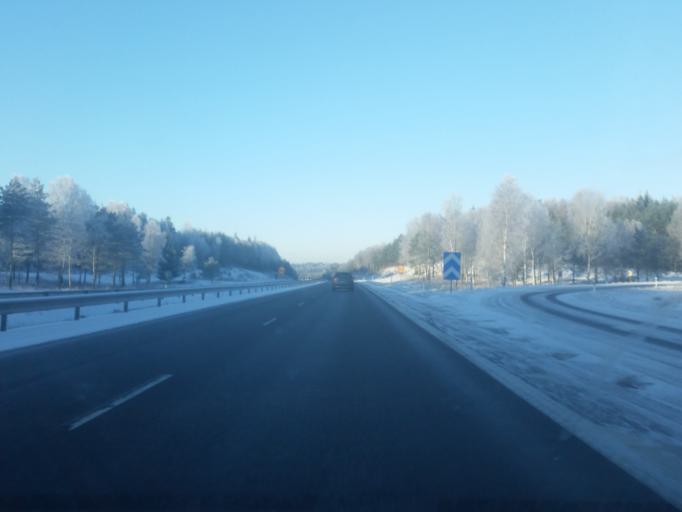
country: SE
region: Vaestra Goetaland
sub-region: Harryda Kommun
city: Hindas
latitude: 57.6747
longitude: 12.3528
